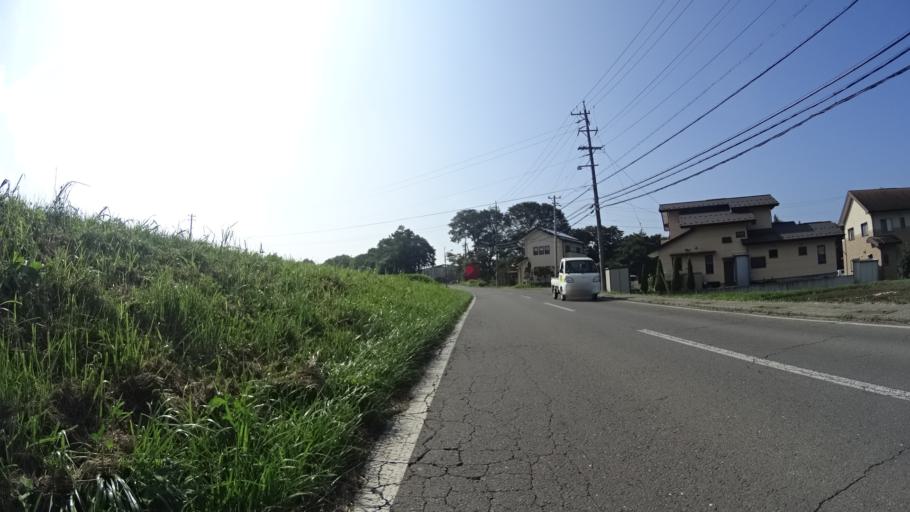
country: JP
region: Nagano
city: Chino
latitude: 35.9624
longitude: 138.2204
